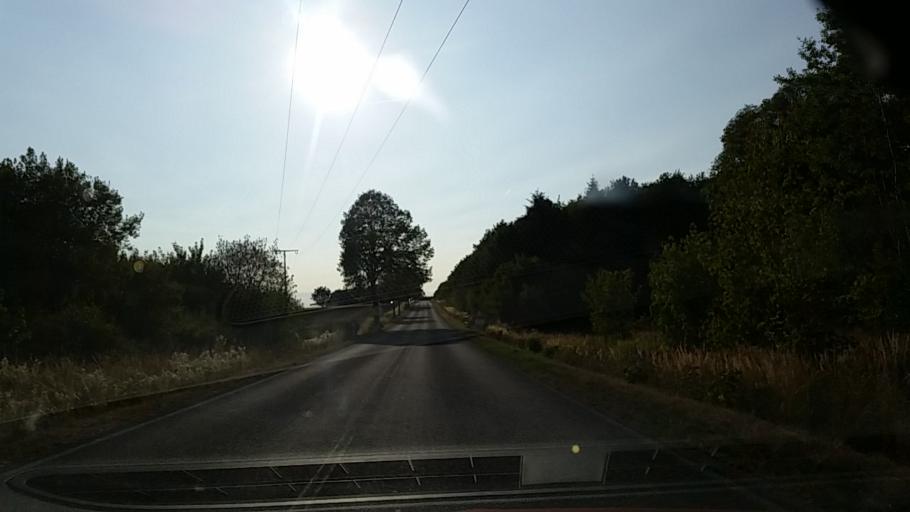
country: DE
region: Lower Saxony
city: Lehre
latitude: 52.2960
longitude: 10.7118
